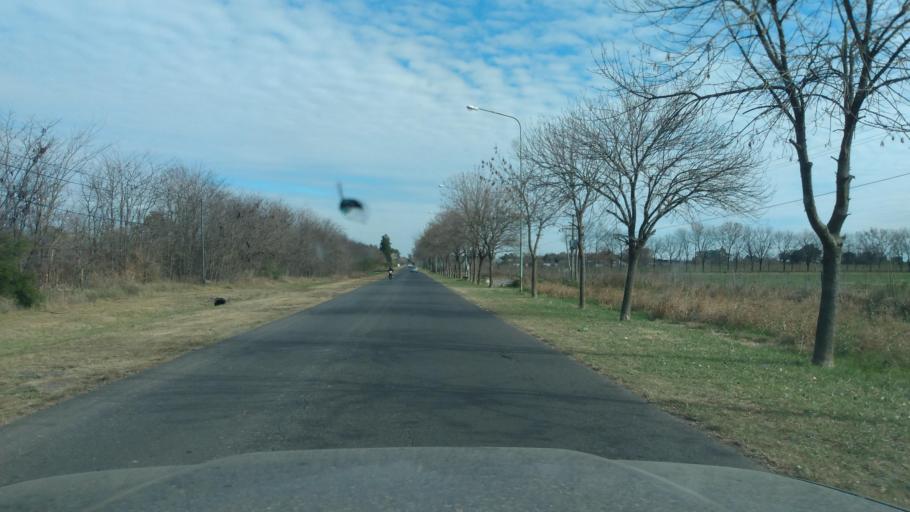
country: AR
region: Buenos Aires
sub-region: Partido de Lujan
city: Lujan
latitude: -34.5758
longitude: -59.1637
